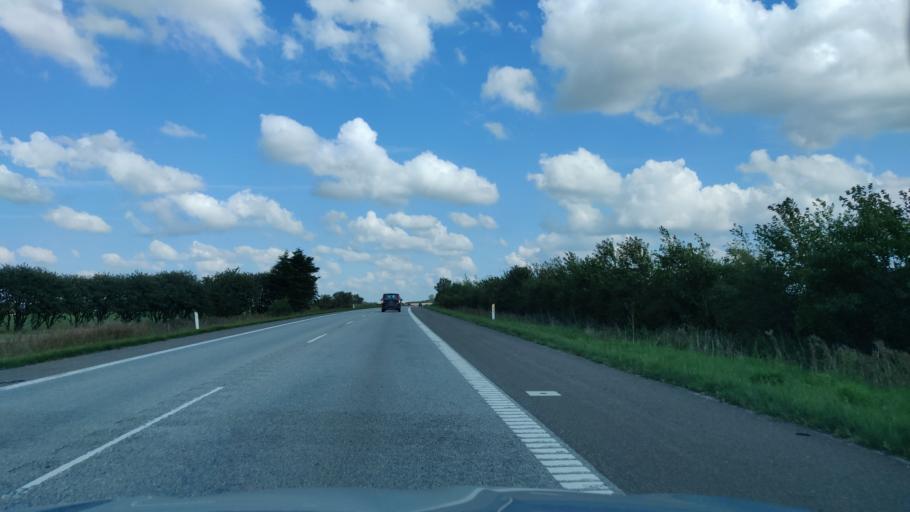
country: DK
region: North Denmark
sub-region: Vesthimmerland Kommune
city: Aars
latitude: 56.8123
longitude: 9.6601
